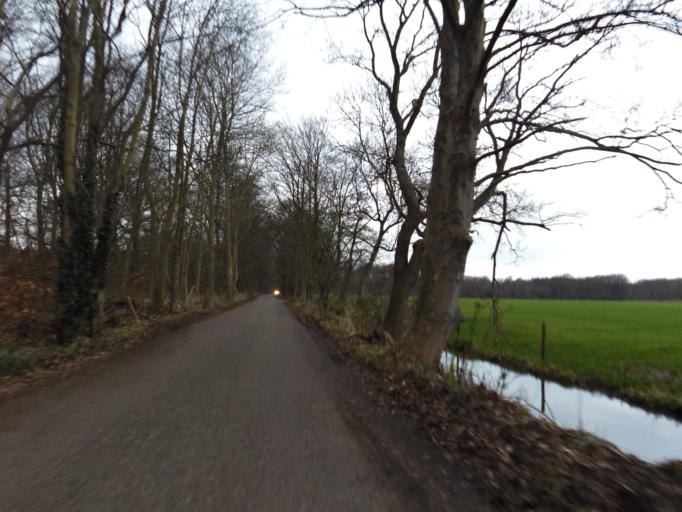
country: NL
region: North Holland
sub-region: Gemeente Bloemendaal
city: Bennebroek
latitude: 52.3295
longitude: 4.5726
